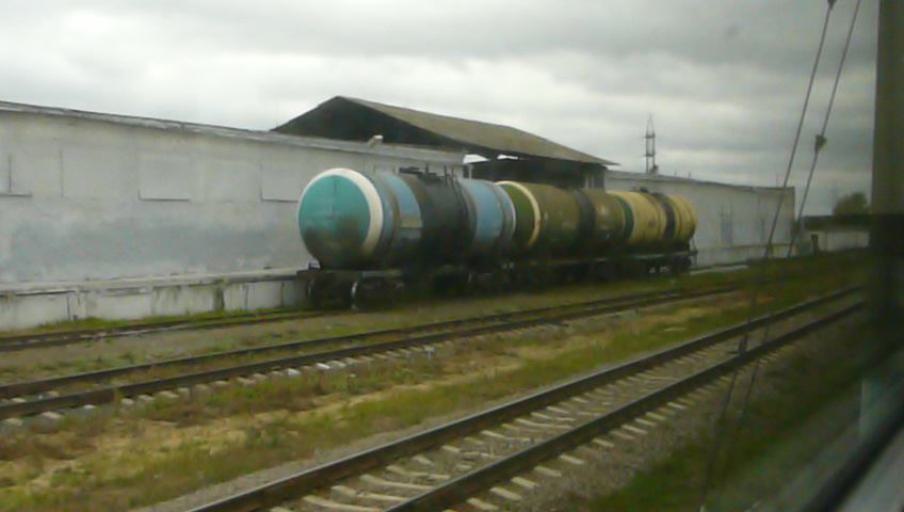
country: RU
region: Moskovskaya
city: Yegor'yevsk
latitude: 55.3949
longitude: 39.0051
